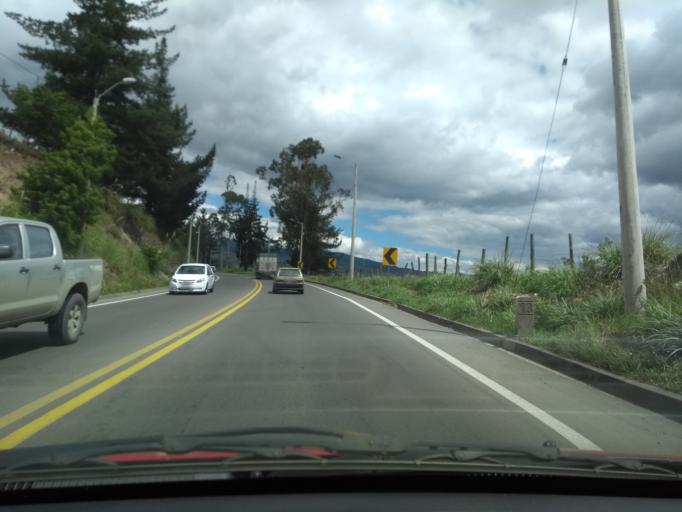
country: EC
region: Azuay
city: Cuenca
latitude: -3.0311
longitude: -79.0412
